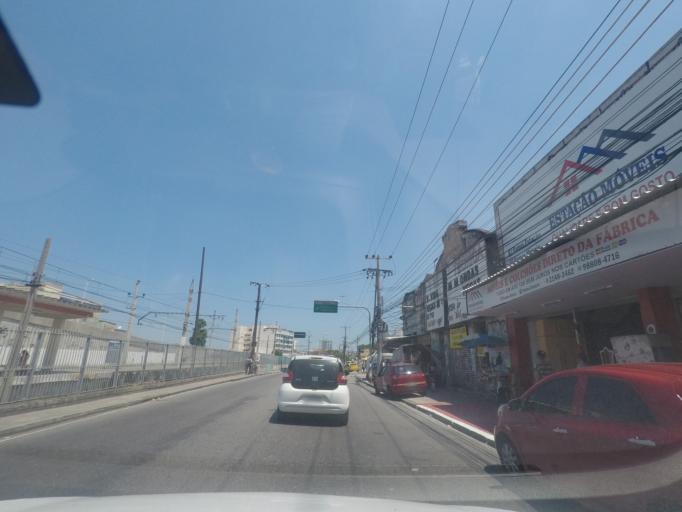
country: BR
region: Rio de Janeiro
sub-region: Rio De Janeiro
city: Rio de Janeiro
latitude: -22.8555
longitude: -43.2600
